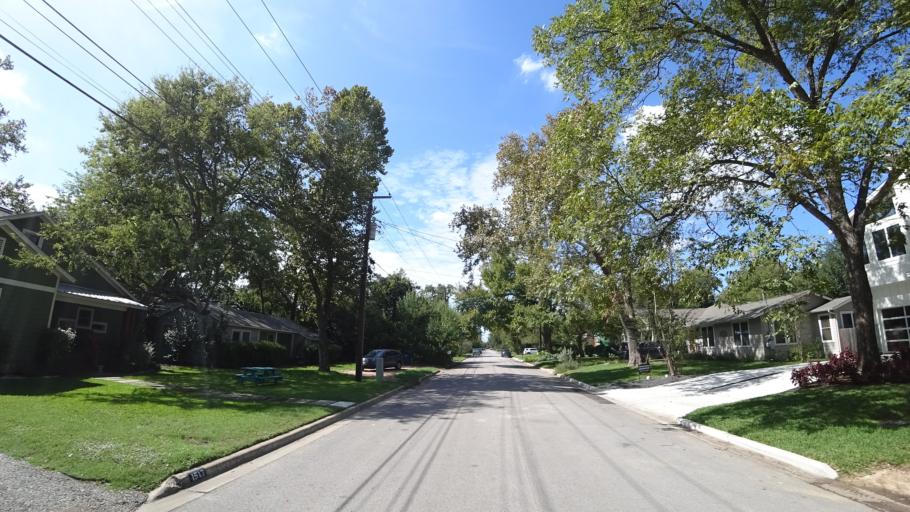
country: US
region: Texas
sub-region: Travis County
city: Austin
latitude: 30.3435
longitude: -97.7280
